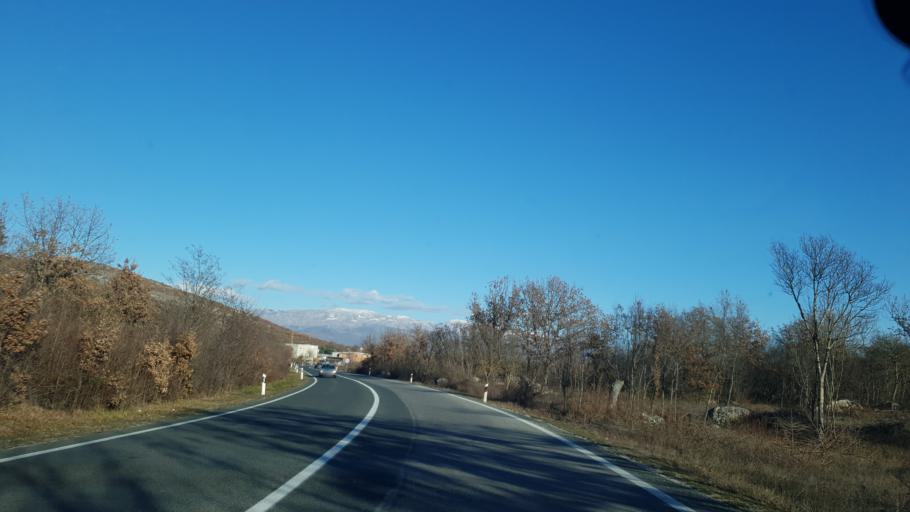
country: HR
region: Splitsko-Dalmatinska
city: Brnaze
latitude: 43.6428
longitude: 16.6181
